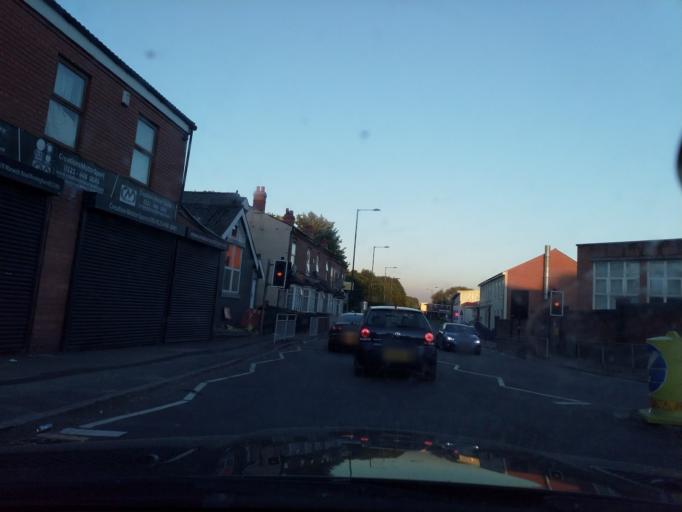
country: GB
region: England
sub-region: City and Borough of Birmingham
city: Acocks Green
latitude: 52.4549
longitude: -1.8580
